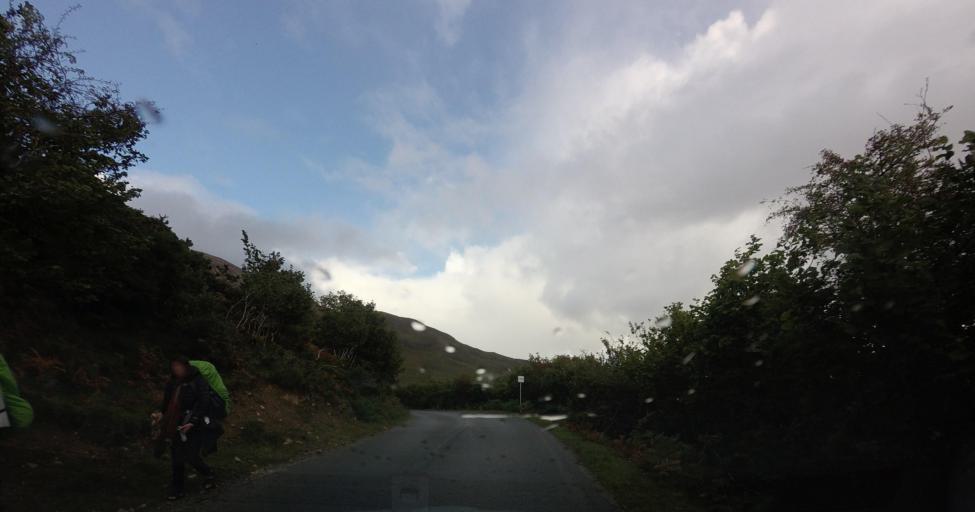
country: GB
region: Scotland
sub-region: Highland
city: Portree
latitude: 57.2104
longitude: -6.0022
